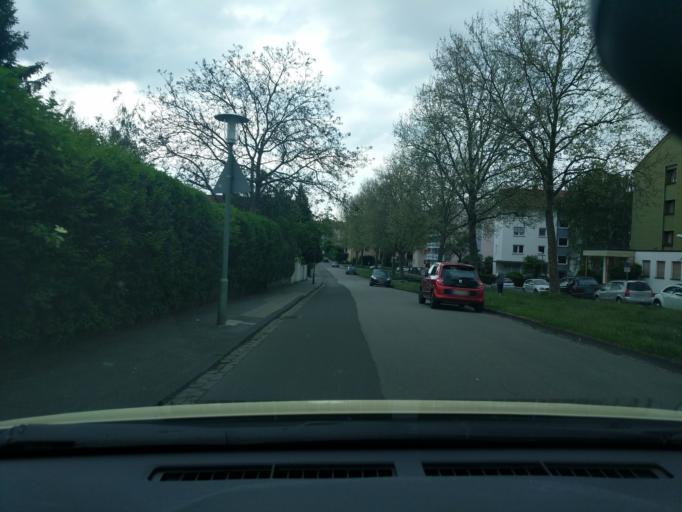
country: DE
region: Rheinland-Pfalz
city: Kaiserslautern
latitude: 49.4488
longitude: 7.7910
